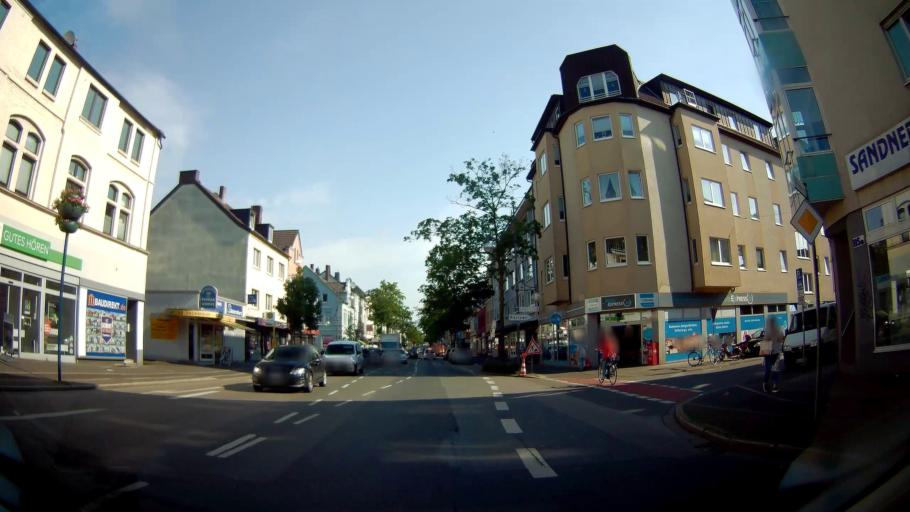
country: DE
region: North Rhine-Westphalia
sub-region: Regierungsbezirk Arnsberg
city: Herne
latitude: 51.5730
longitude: 7.2125
